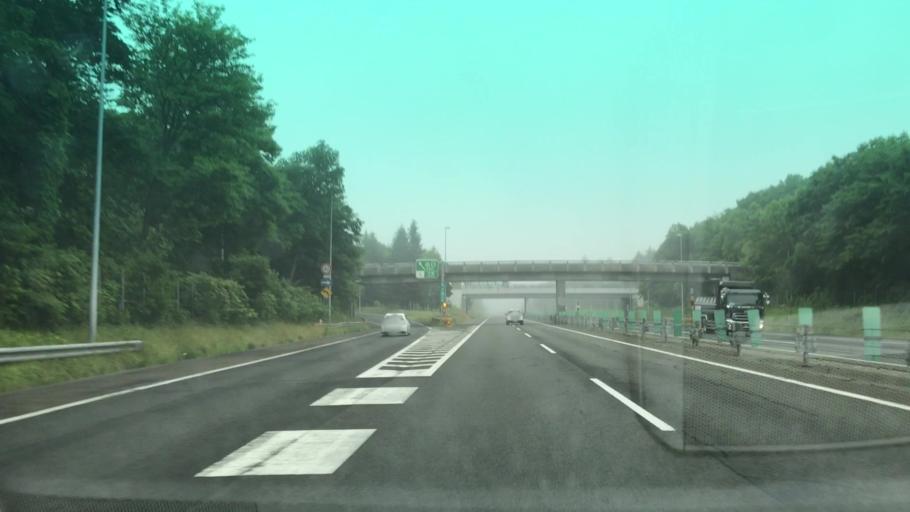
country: JP
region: Hokkaido
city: Chitose
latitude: 42.8136
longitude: 141.6203
